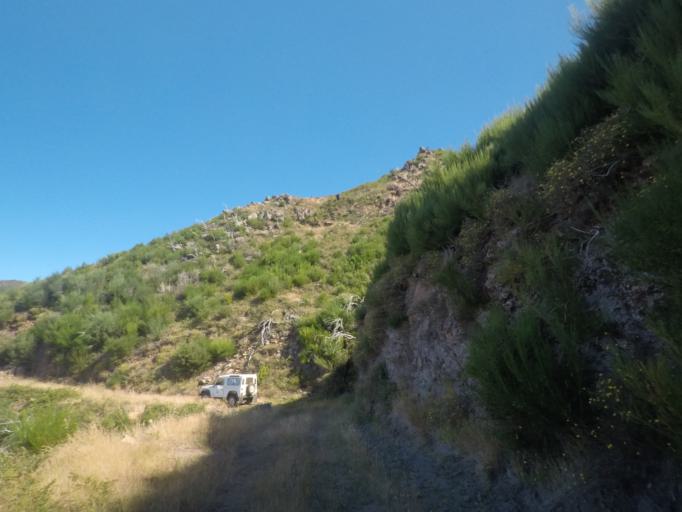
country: PT
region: Madeira
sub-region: Funchal
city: Nossa Senhora do Monte
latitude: 32.7067
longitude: -16.9168
